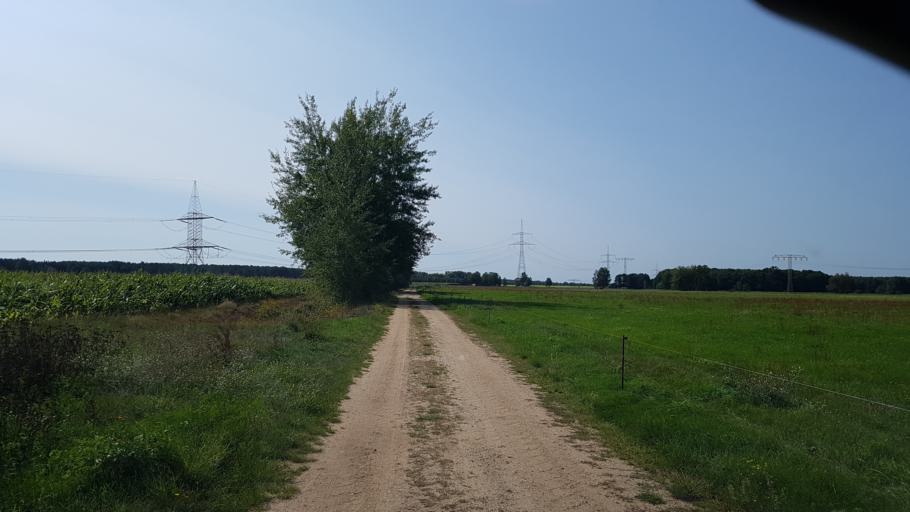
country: DE
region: Brandenburg
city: Sonnewalde
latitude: 51.6626
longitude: 13.6326
